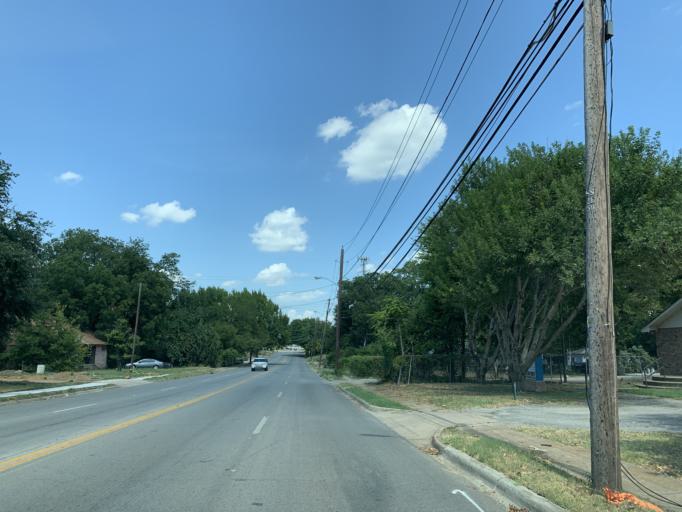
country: US
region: Texas
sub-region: Dallas County
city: Dallas
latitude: 32.7124
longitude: -96.7819
